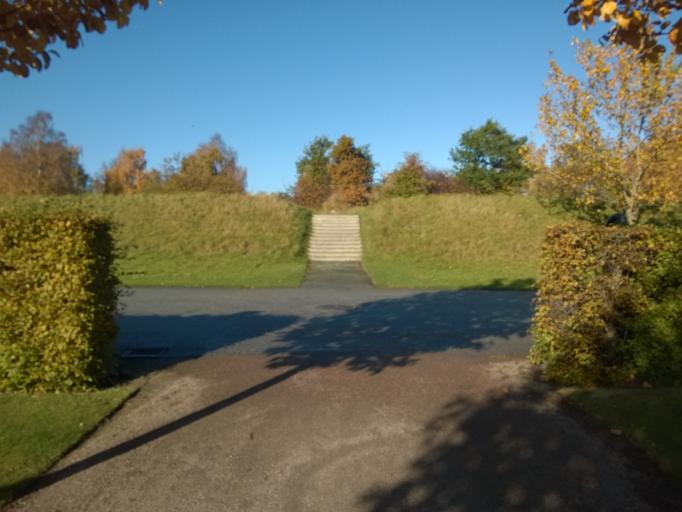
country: SE
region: Skane
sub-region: Malmo
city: Malmoe
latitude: 55.5938
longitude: 13.0443
